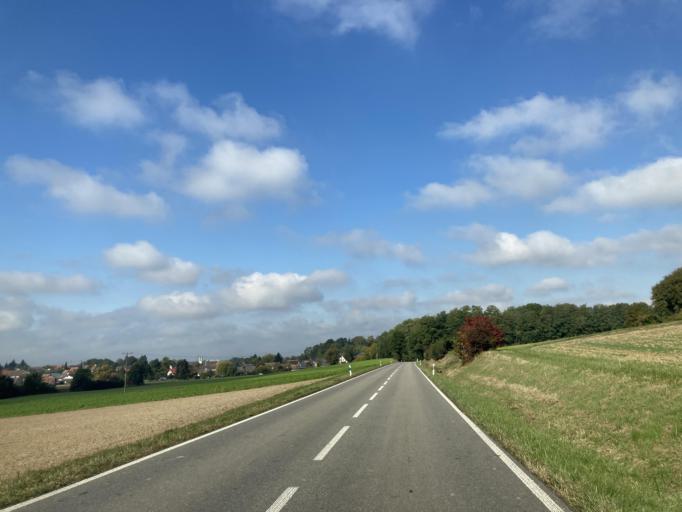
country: DE
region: Baden-Wuerttemberg
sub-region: Freiburg Region
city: Buggingen
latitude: 47.8405
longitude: 7.6476
